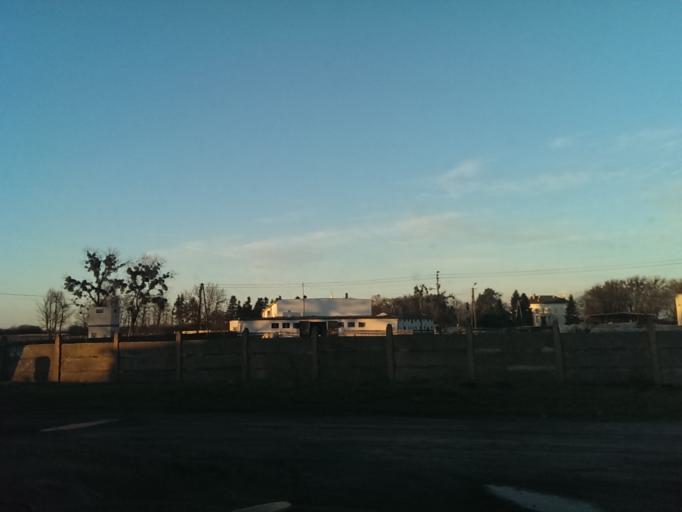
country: PL
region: Kujawsko-Pomorskie
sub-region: Powiat nakielski
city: Szubin
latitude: 53.0728
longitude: 17.6904
